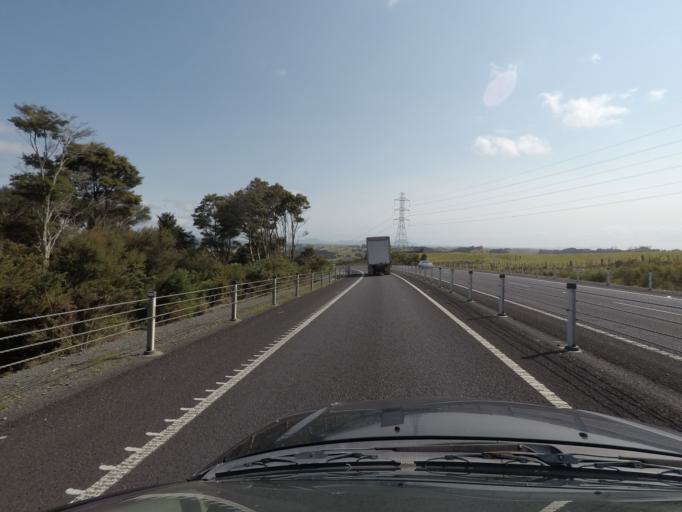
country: NZ
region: Northland
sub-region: Whangarei
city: Ruakaka
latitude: -36.0471
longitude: 174.4170
